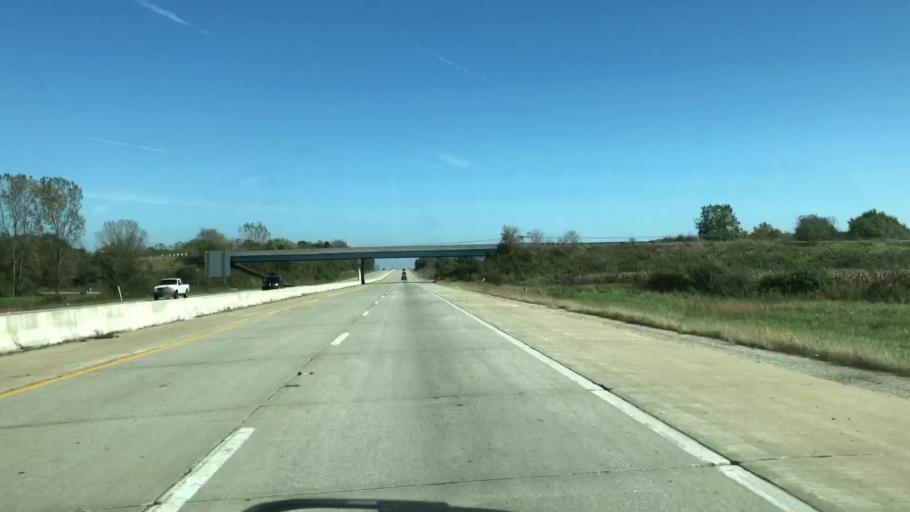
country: US
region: Indiana
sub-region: Elkhart County
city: Elkhart
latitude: 41.6351
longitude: -85.9864
